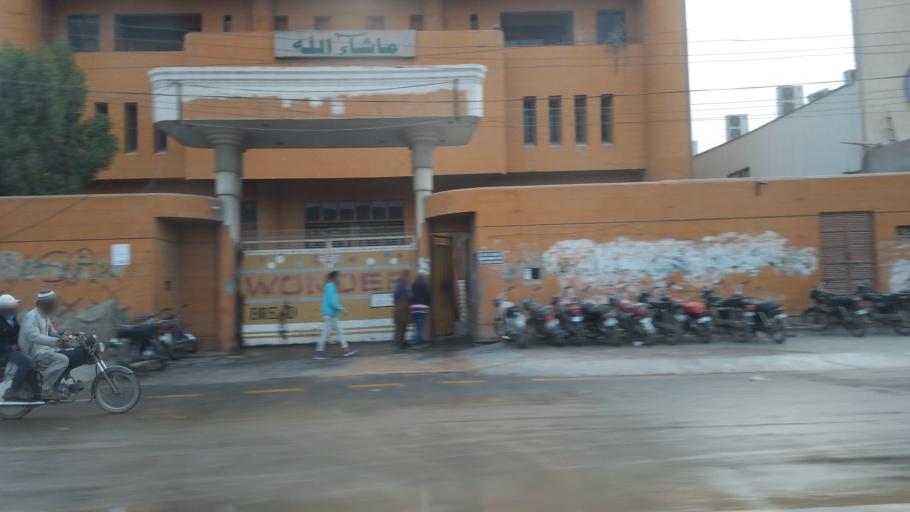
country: PK
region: Sindh
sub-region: Karachi District
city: Karachi
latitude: 24.9398
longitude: 67.0852
